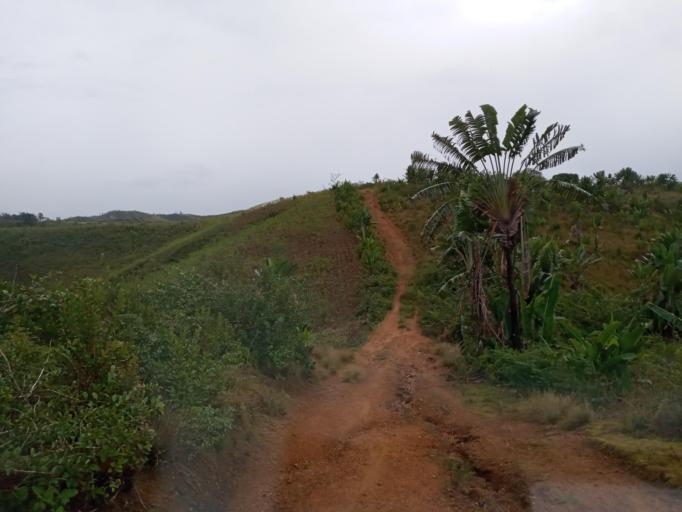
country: MG
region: Atsimo-Atsinanana
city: Vohipaho
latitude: -24.0062
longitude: 47.4108
